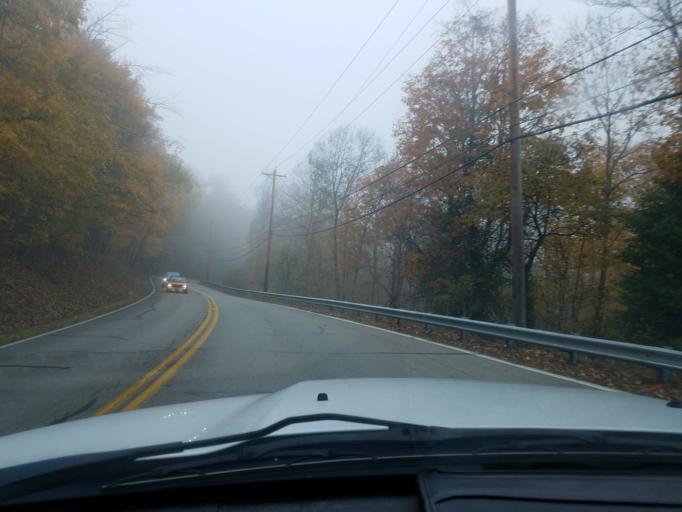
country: US
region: Indiana
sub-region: Floyd County
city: New Albany
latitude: 38.3184
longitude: -85.8545
